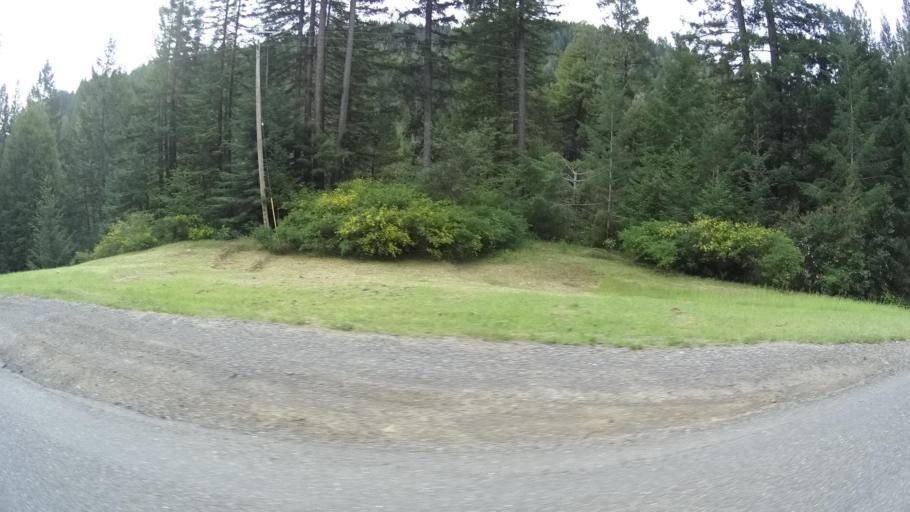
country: US
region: California
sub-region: Humboldt County
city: Redway
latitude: 40.2824
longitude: -123.8459
